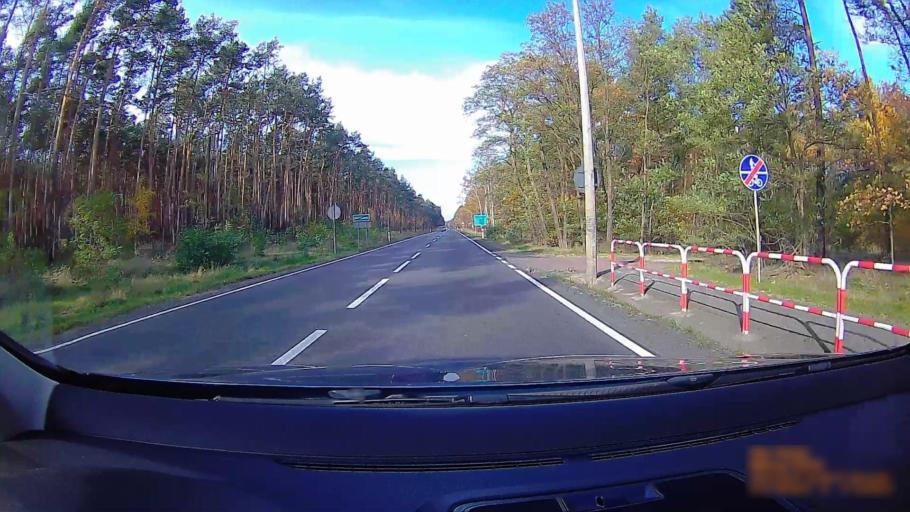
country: PL
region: Greater Poland Voivodeship
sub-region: Powiat ostrzeszowski
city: Ostrzeszow
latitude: 51.4473
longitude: 17.9102
